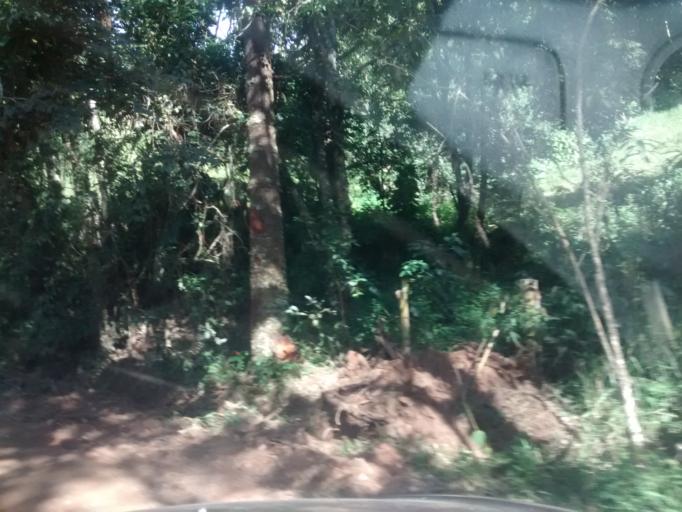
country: BR
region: Sao Paulo
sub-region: Campos Do Jordao
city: Campos do Jordao
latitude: -22.7395
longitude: -45.6664
